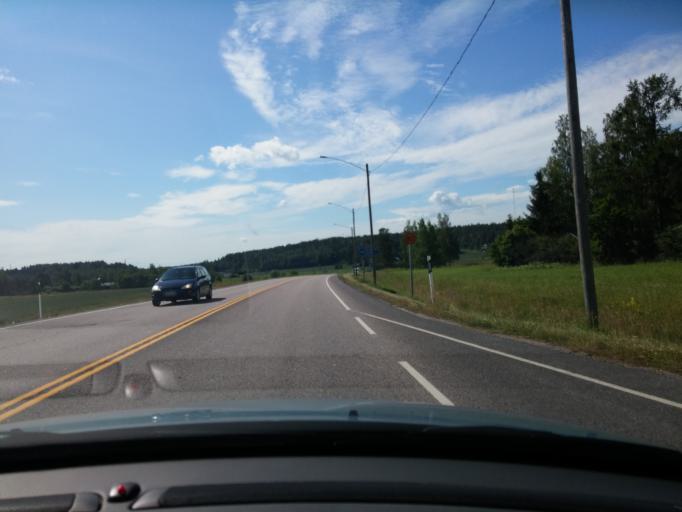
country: FI
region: Uusimaa
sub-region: Porvoo
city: Askola
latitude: 60.4482
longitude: 25.5856
